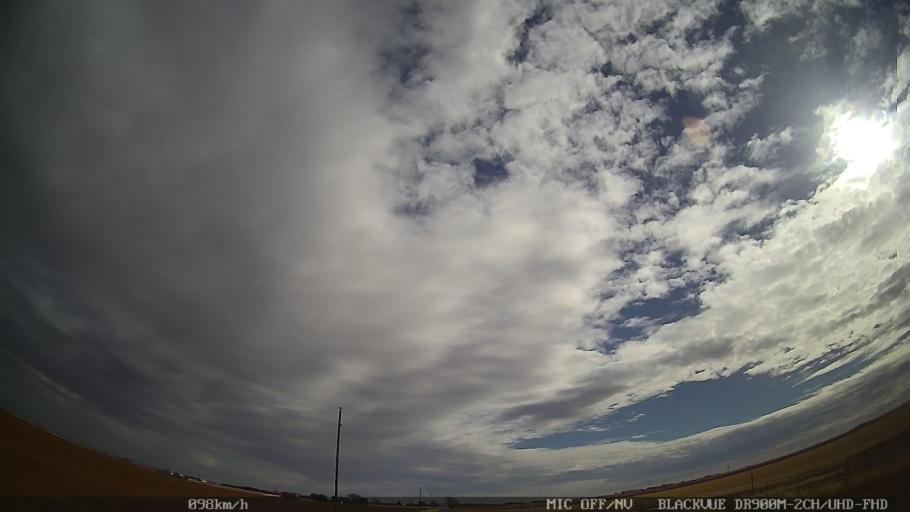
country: US
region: New Mexico
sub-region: Curry County
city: Clovis
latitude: 34.4194
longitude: -103.1308
